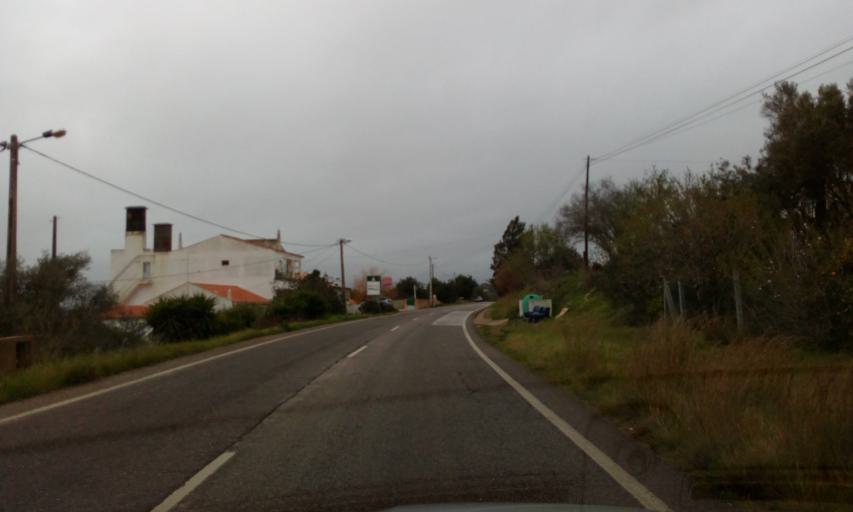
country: PT
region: Faro
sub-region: Albufeira
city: Guia
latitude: 37.1707
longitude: -8.3289
